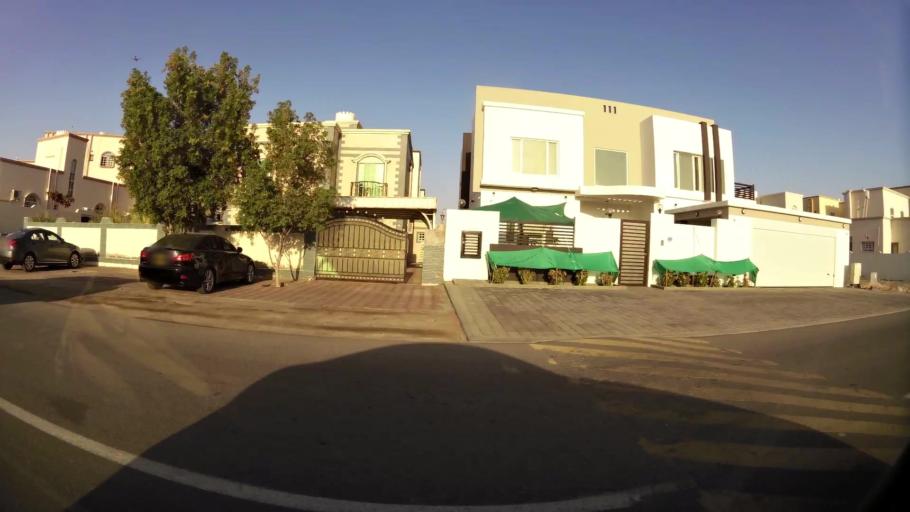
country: OM
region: Muhafazat Masqat
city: As Sib al Jadidah
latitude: 23.5926
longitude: 58.1383
